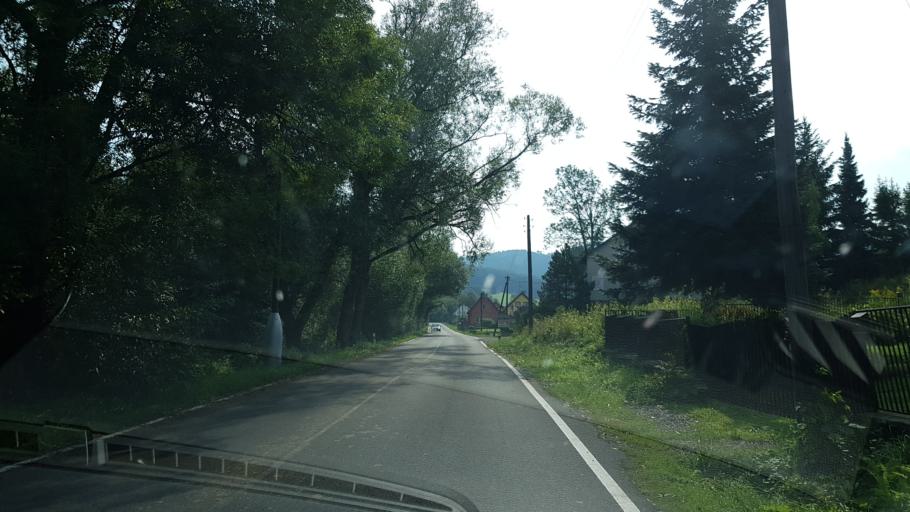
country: CZ
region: Olomoucky
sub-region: Okres Jesenik
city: Jesenik
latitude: 50.2164
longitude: 17.2163
